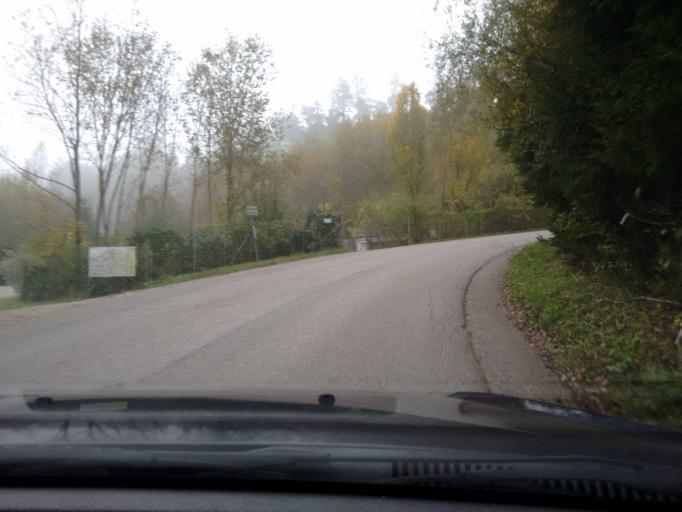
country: AT
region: Upper Austria
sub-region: Wels-Land
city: Buchkirchen
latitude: 48.1931
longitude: 13.9694
